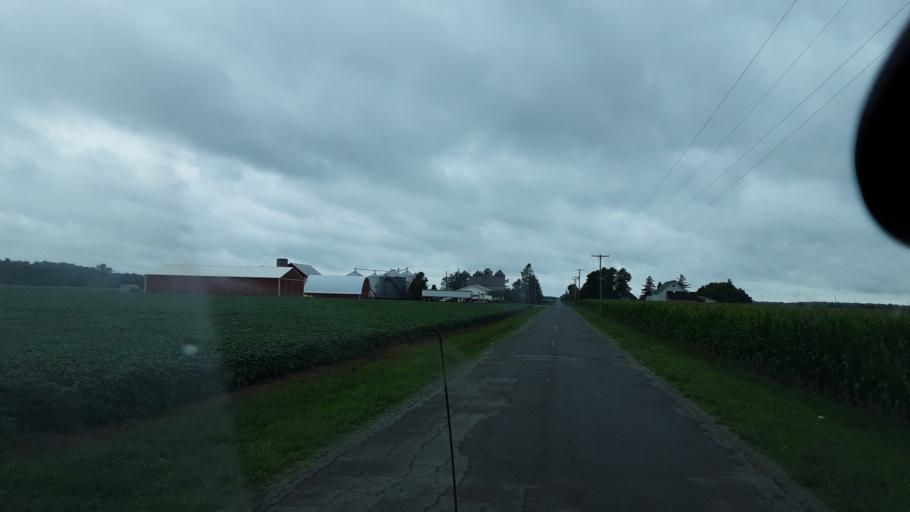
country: US
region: Ohio
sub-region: Van Wert County
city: Convoy
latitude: 40.8223
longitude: -84.6837
